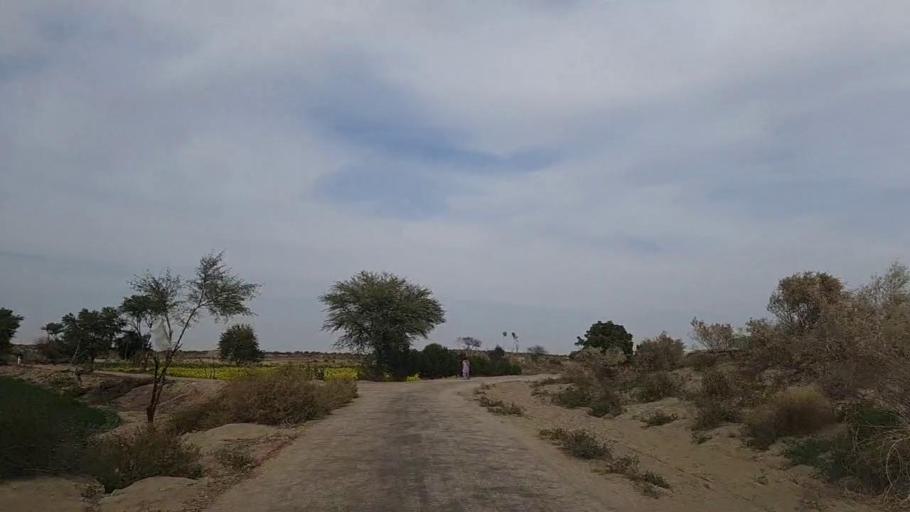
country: PK
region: Sindh
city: Jam Sahib
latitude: 26.4454
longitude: 68.6125
